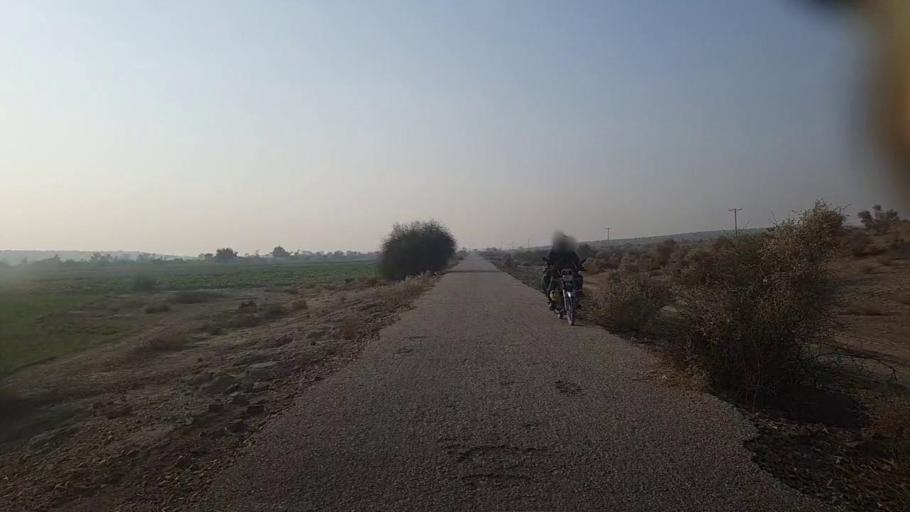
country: PK
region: Sindh
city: Pad Idan
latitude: 26.7134
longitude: 68.4722
